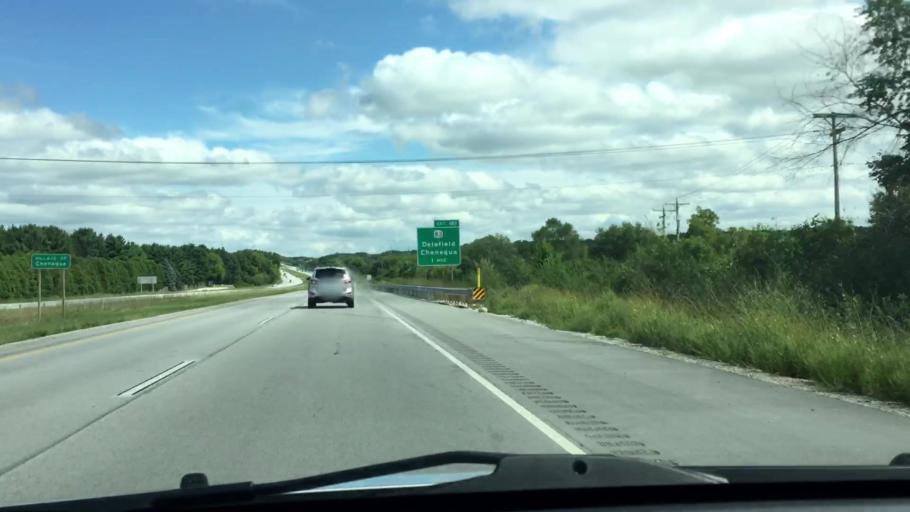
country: US
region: Wisconsin
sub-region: Waukesha County
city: Nashotah
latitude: 43.1019
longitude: -88.3934
